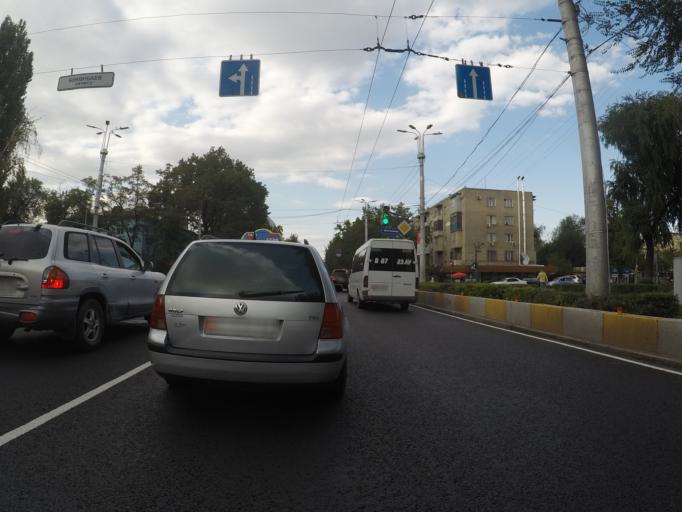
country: KG
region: Chuy
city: Bishkek
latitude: 42.8673
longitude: 74.5875
